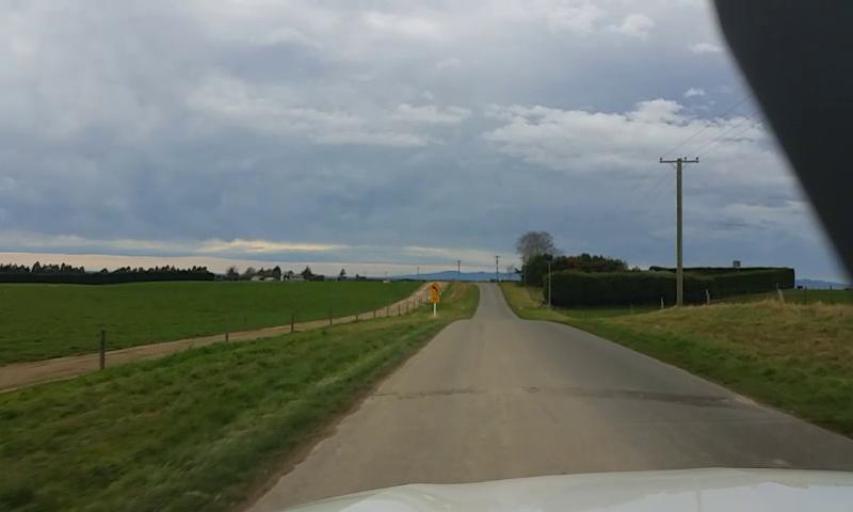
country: NZ
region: Canterbury
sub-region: Waimakariri District
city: Kaiapoi
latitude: -43.2953
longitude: 172.4749
